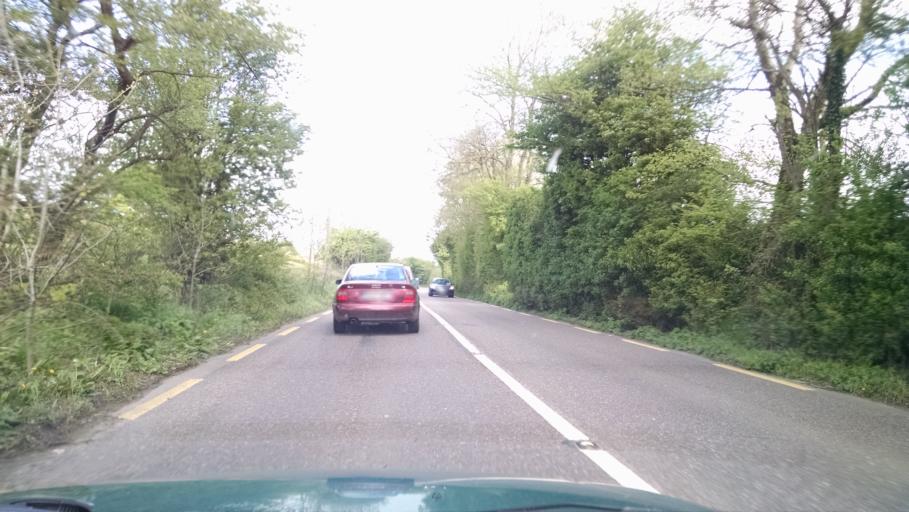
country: IE
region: Munster
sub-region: County Cork
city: Carrigaline
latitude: 51.8541
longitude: -8.4197
